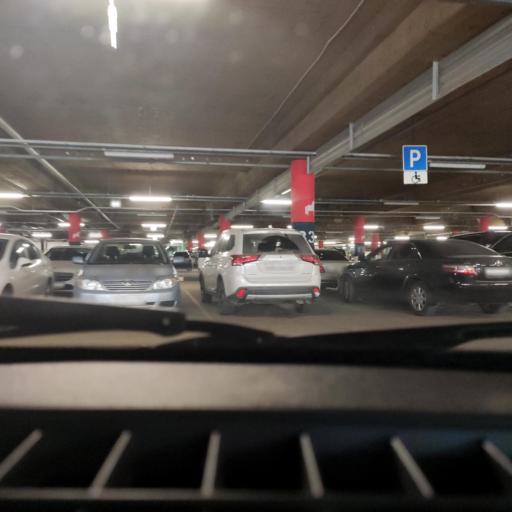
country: RU
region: Bashkortostan
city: Ufa
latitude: 54.6748
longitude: 55.9310
